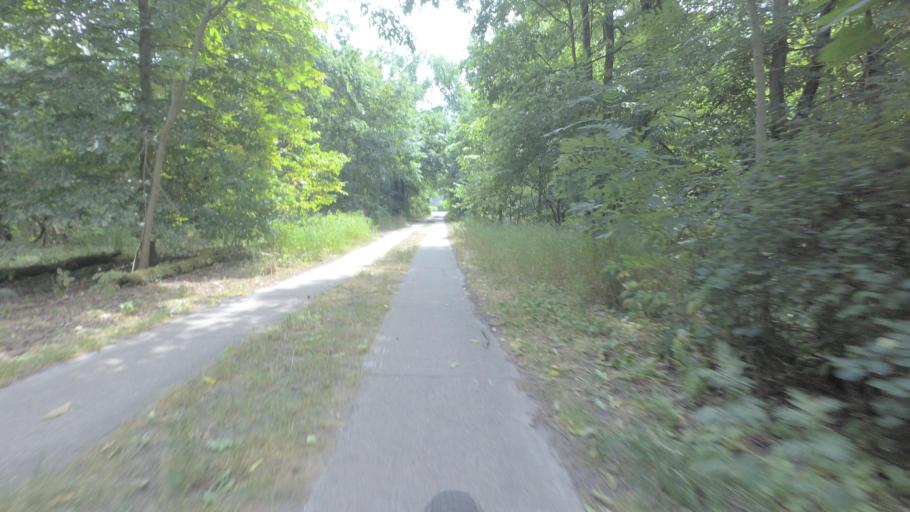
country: DE
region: Brandenburg
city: Stahnsdorf
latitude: 52.3407
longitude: 13.2260
